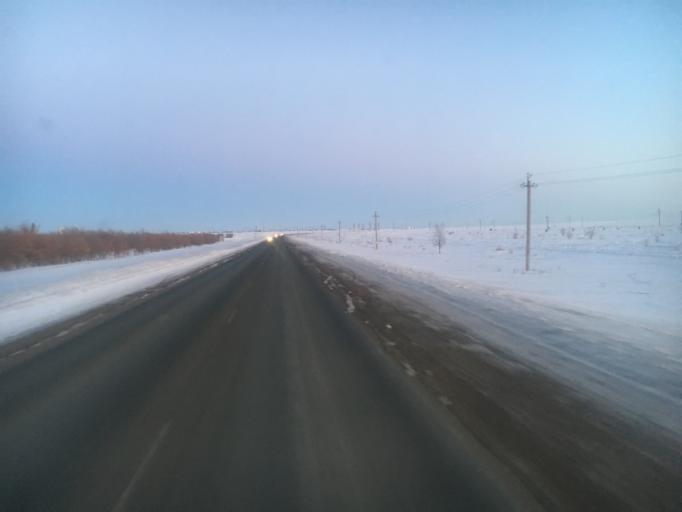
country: KZ
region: Batys Qazaqstan
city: Krugloozernoe
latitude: 51.1487
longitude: 51.3141
